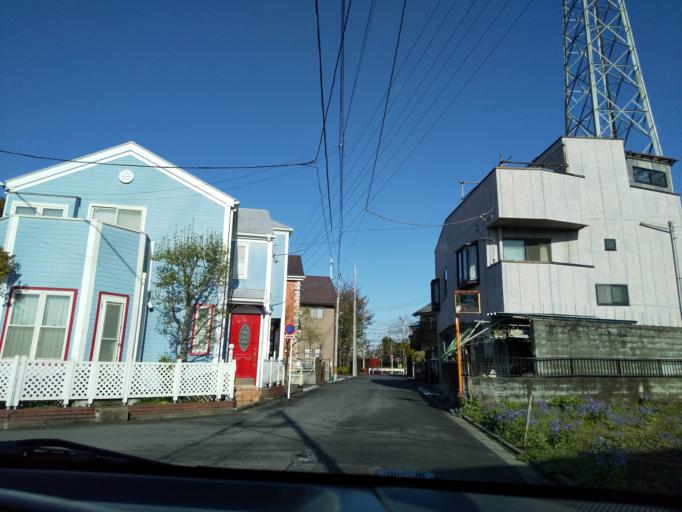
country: JP
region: Tokyo
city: Hino
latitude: 35.6898
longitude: 139.4332
